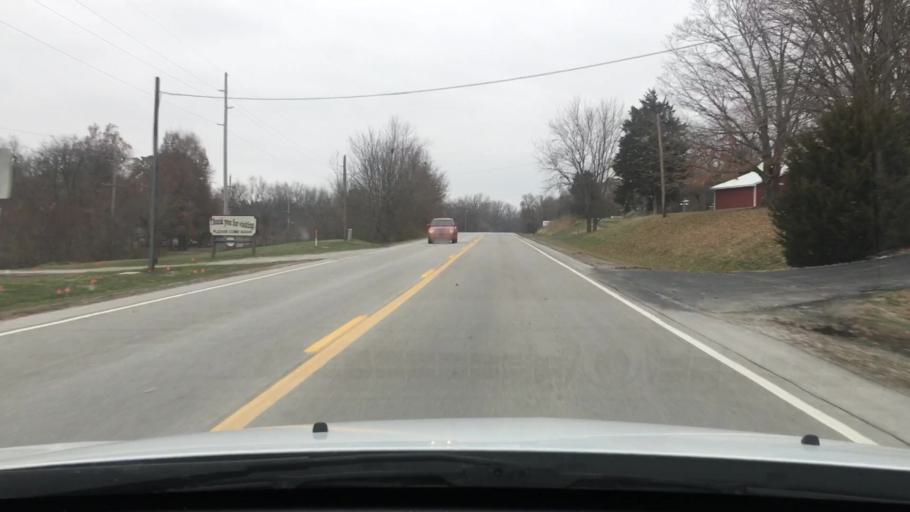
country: US
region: Illinois
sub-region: Pike County
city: Pittsfield
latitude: 39.6193
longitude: -90.8014
